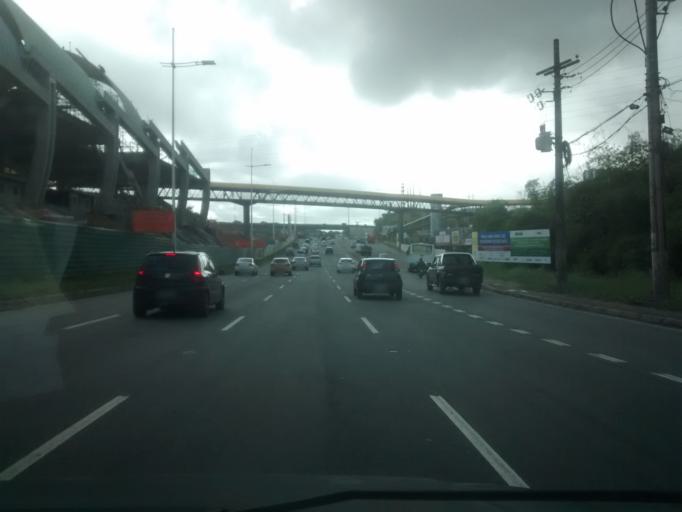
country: BR
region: Bahia
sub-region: Salvador
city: Salvador
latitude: -12.9461
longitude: -38.4214
